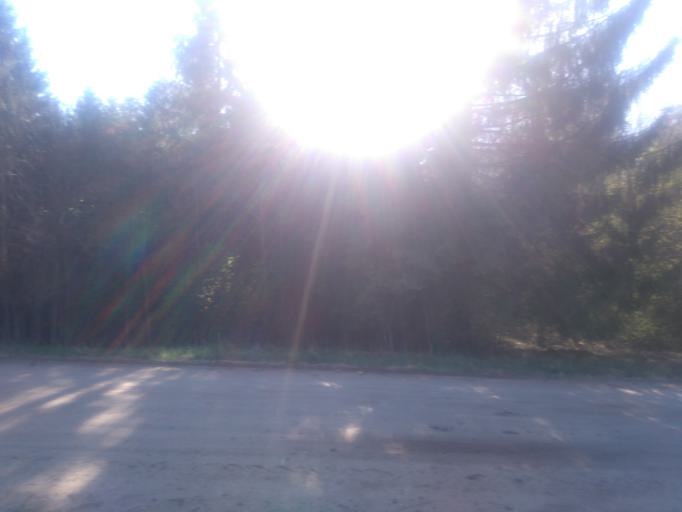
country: LV
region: Vecpiebalga
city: Vecpiebalga
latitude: 57.0108
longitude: 25.8403
